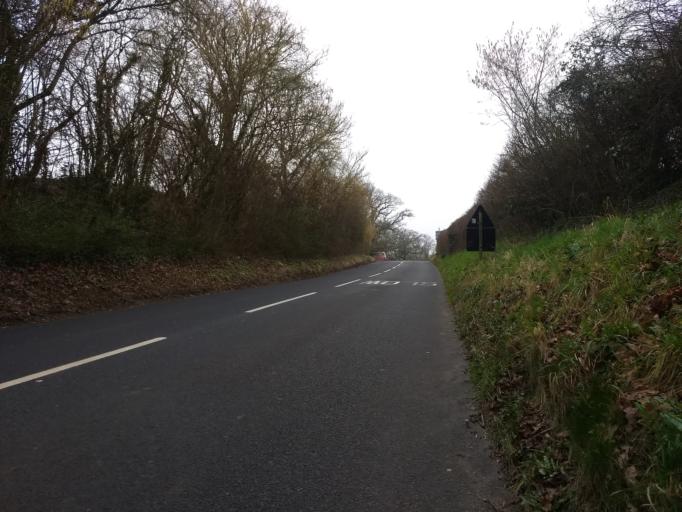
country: GB
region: England
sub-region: Isle of Wight
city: Newchurch
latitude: 50.7048
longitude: -1.2144
